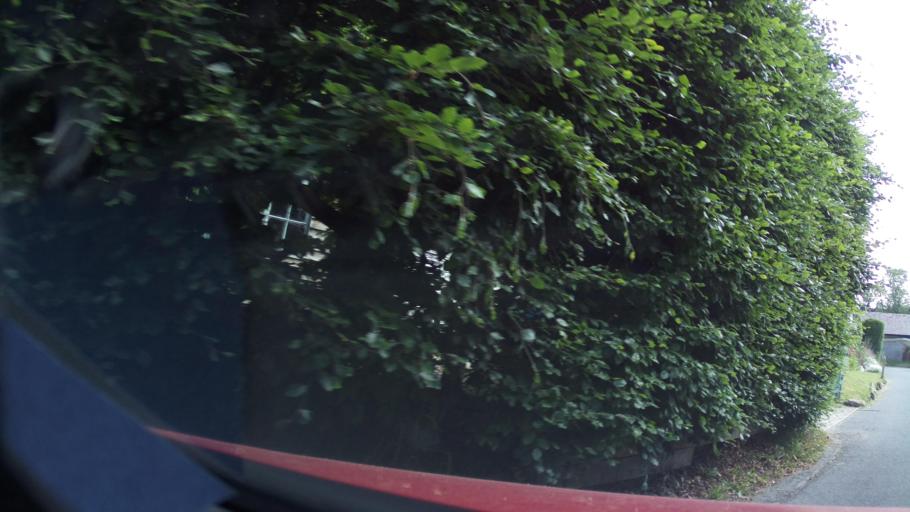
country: GB
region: England
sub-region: Wiltshire
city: Rushall
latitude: 51.2606
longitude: -1.7989
